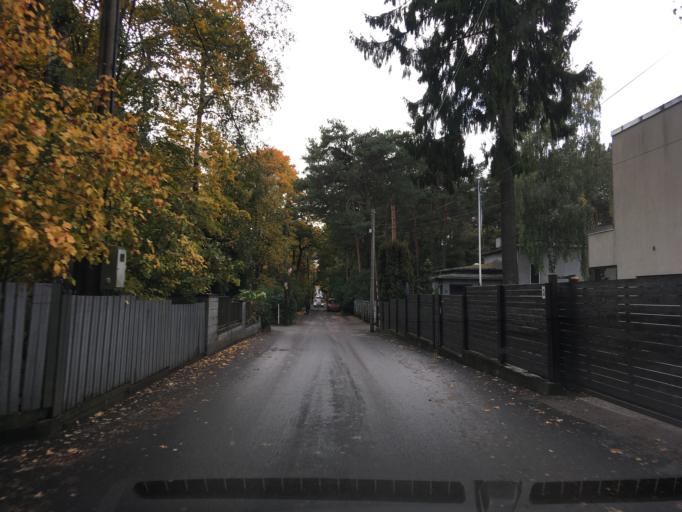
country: EE
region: Harju
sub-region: Tallinna linn
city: Tallinn
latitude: 59.3859
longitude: 24.6971
